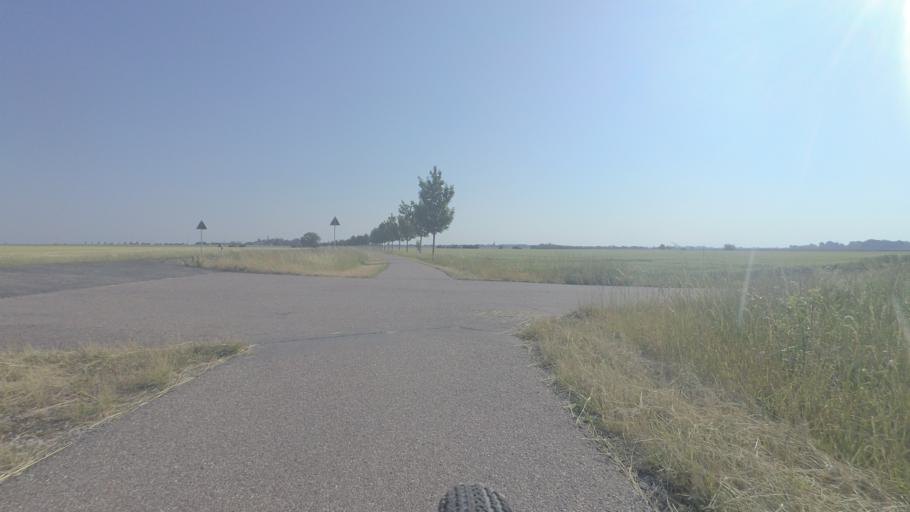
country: DE
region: Saxony-Anhalt
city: Osternienburger Land
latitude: 51.7810
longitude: 12.0048
